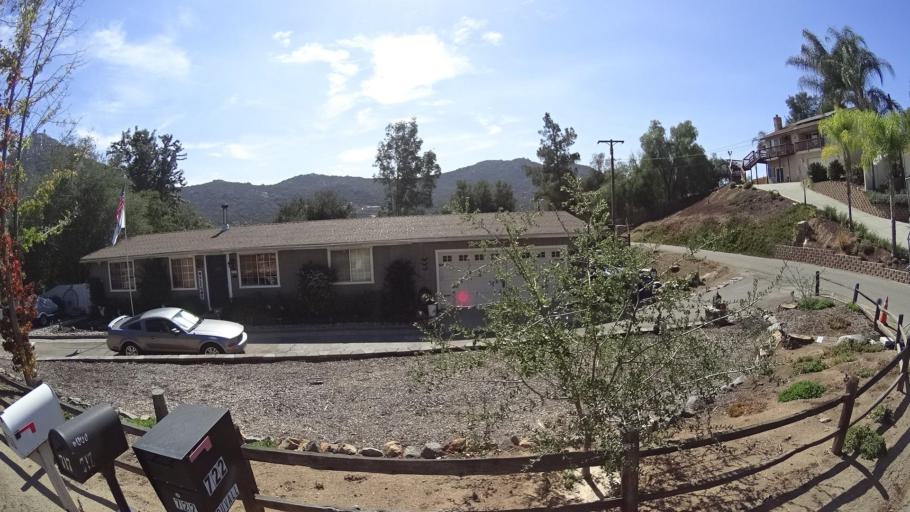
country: US
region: California
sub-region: San Diego County
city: Harbison Canyon
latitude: 32.8183
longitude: -116.8354
